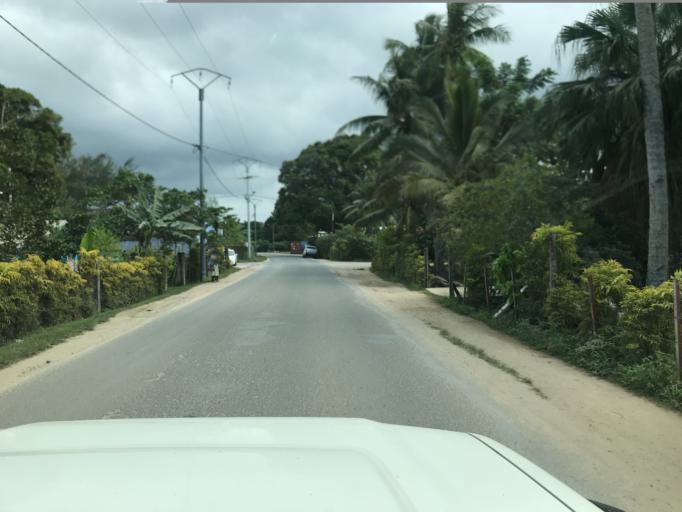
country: VU
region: Sanma
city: Luganville
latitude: -15.5123
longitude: 167.1720
